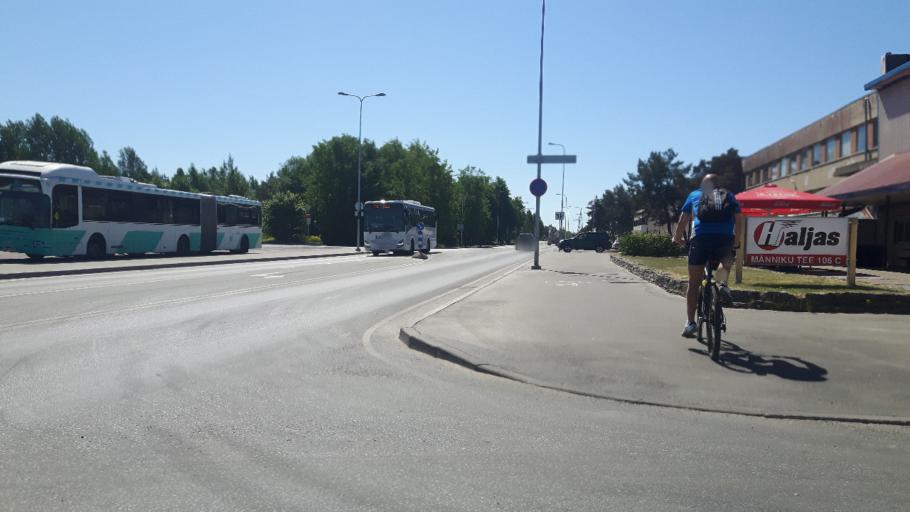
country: EE
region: Harju
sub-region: Tallinna linn
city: Tallinn
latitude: 59.3658
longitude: 24.7176
